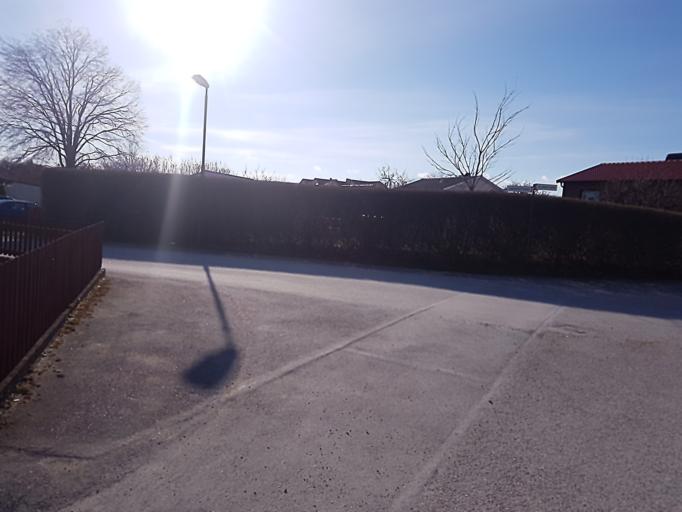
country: SE
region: Gotland
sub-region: Gotland
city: Visby
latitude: 57.6173
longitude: 18.2895
